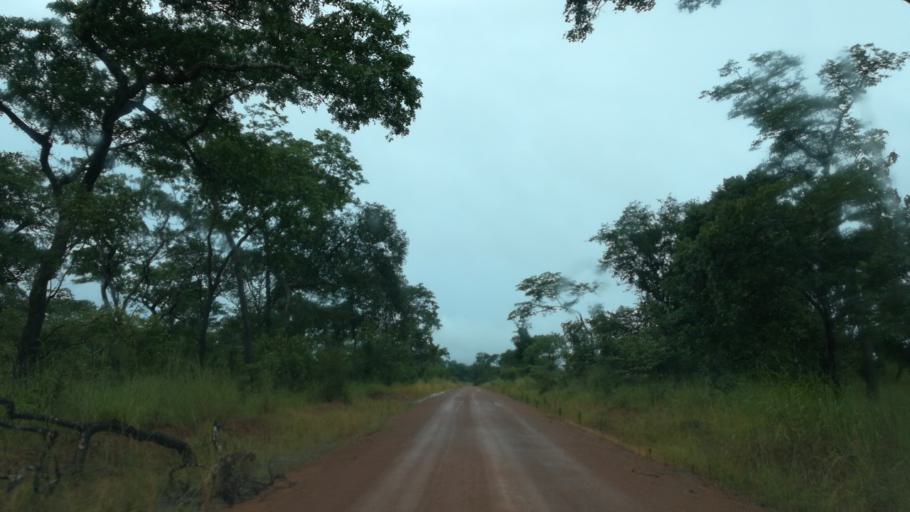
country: ZM
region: Luapula
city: Mwense
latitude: -10.7235
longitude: 28.2141
